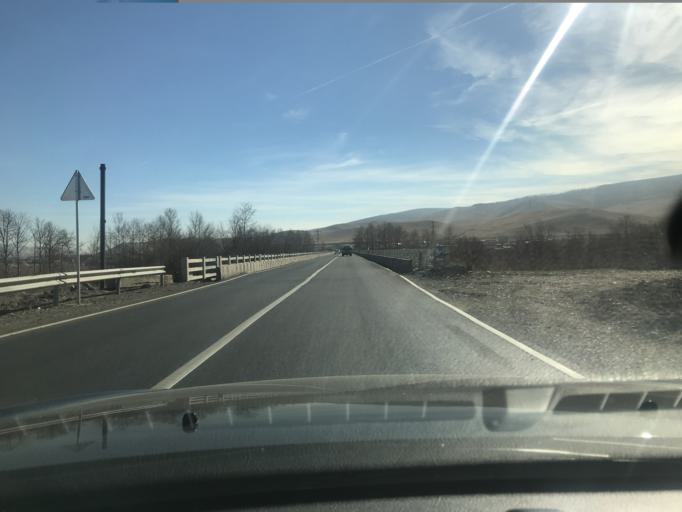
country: MN
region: Ulaanbaatar
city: Ulaanbaatar
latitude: 47.8953
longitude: 107.0641
